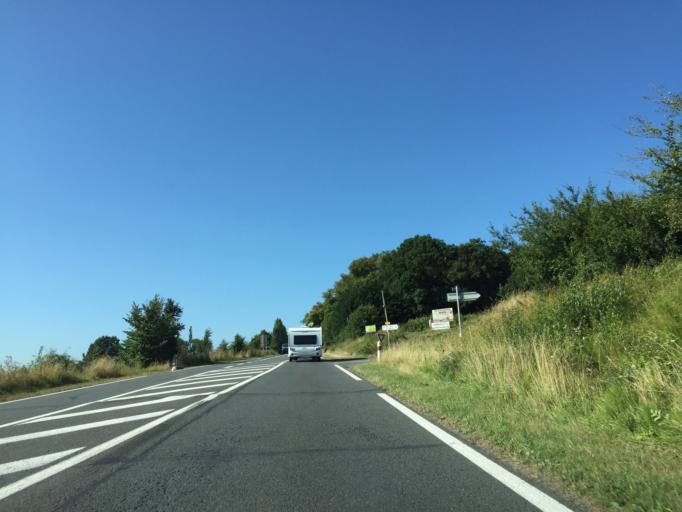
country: FR
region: Lower Normandy
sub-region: Departement du Calvados
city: Saint-Gatien-des-Bois
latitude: 49.2730
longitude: 0.2169
